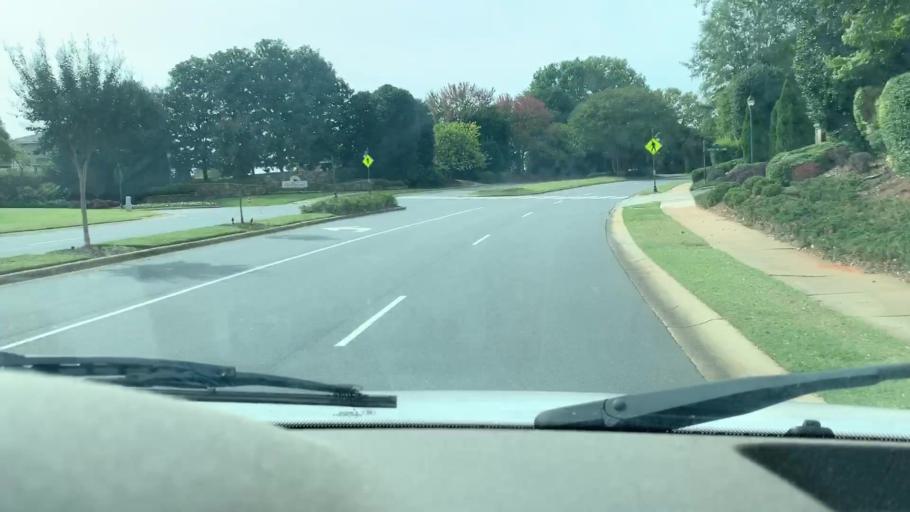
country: US
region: North Carolina
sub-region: Mecklenburg County
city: Cornelius
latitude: 35.4709
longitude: -80.9130
